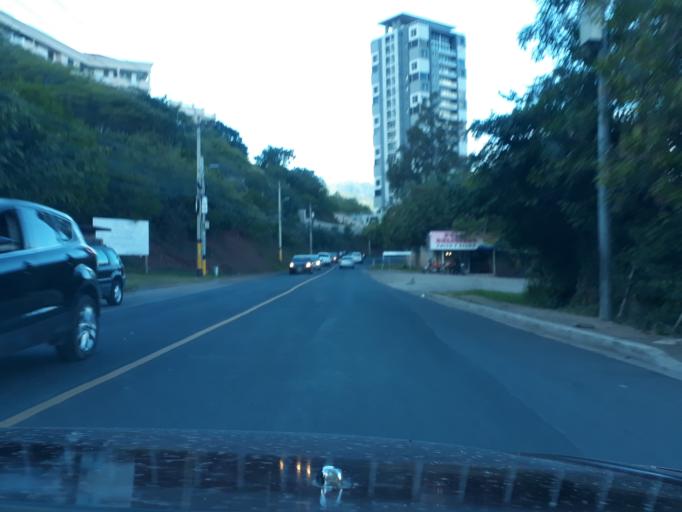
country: HN
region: Francisco Morazan
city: Tegucigalpa
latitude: 14.1098
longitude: -87.1681
